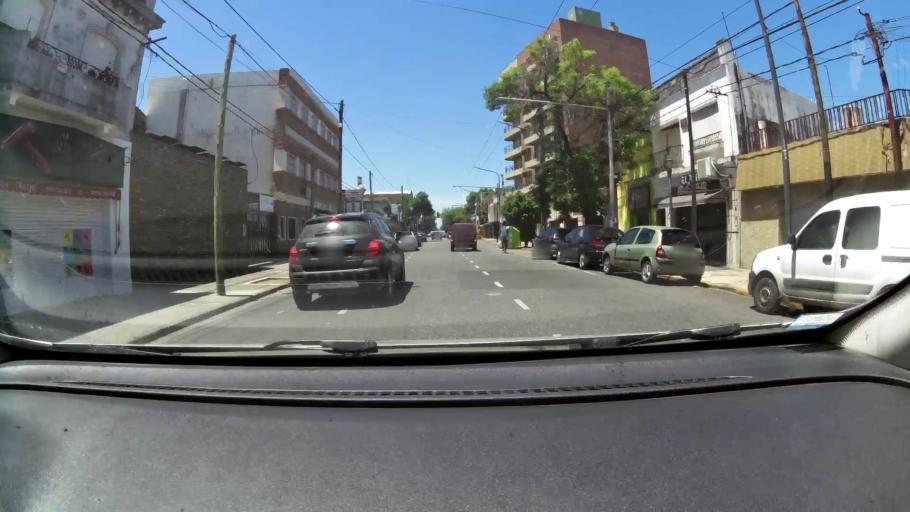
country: AR
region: Santa Fe
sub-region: Departamento de Rosario
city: Rosario
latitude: -32.9415
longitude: -60.6957
